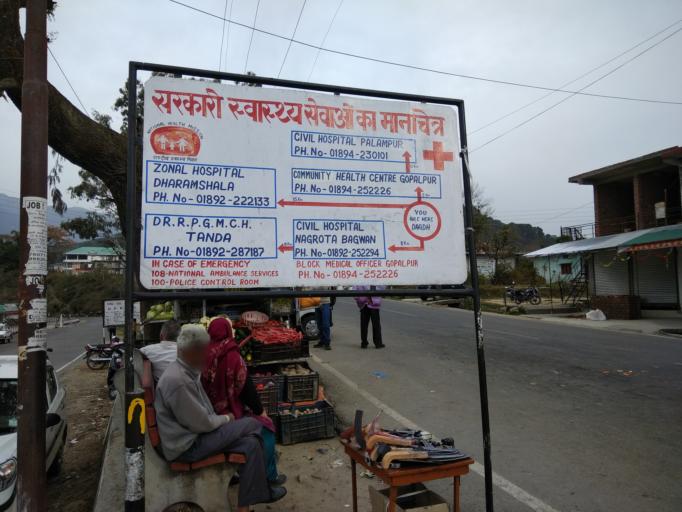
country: IN
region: Himachal Pradesh
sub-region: Kangra
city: Dharmsala
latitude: 32.1470
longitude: 76.4208
